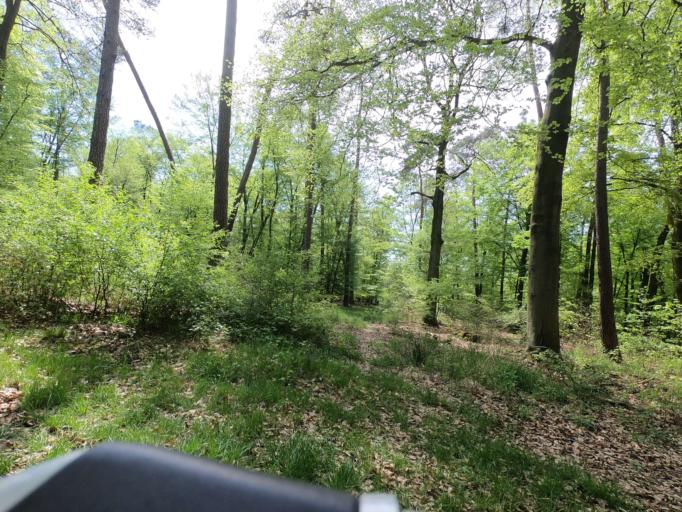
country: DE
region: Hesse
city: Morfelden-Walldorf
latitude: 50.0172
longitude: 8.5645
